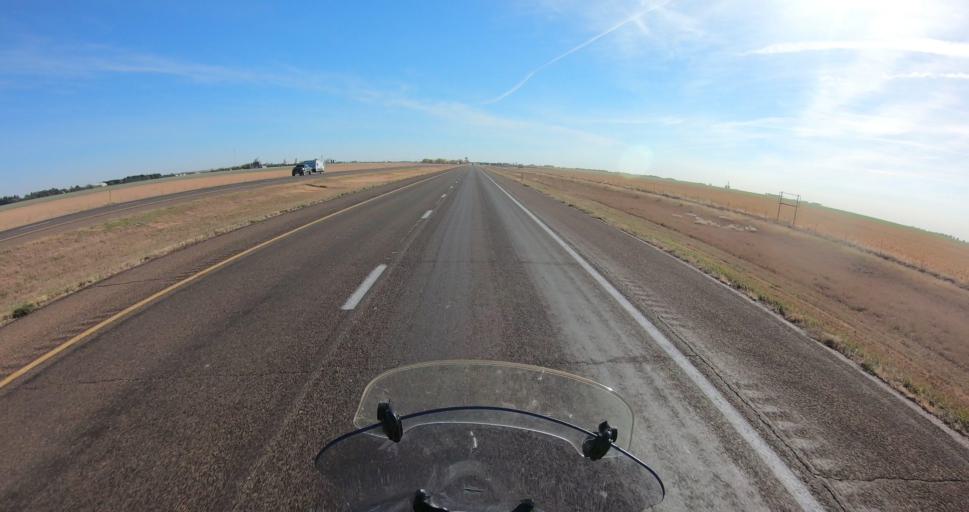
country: US
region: Kansas
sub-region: Sherman County
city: Goodland
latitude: 39.3287
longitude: -101.7609
